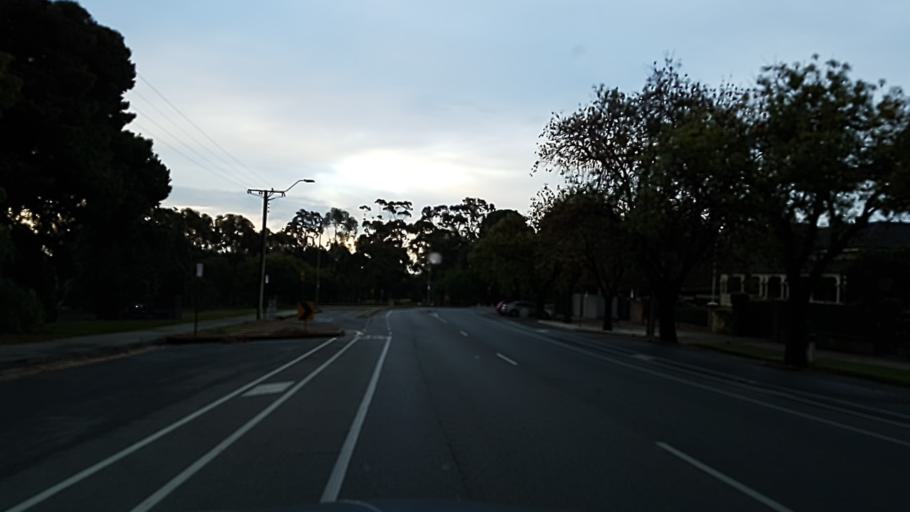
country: AU
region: South Australia
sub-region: Adelaide
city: North Adelaide
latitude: -34.9048
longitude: 138.5858
